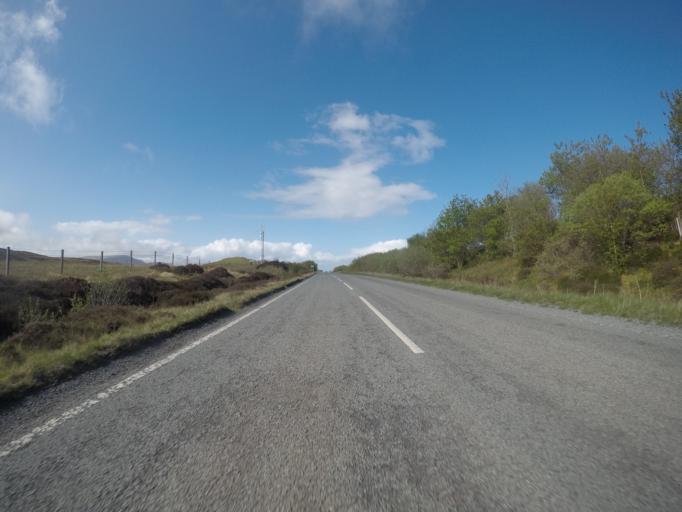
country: GB
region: Scotland
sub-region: Highland
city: Portree
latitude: 57.5878
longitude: -6.1573
